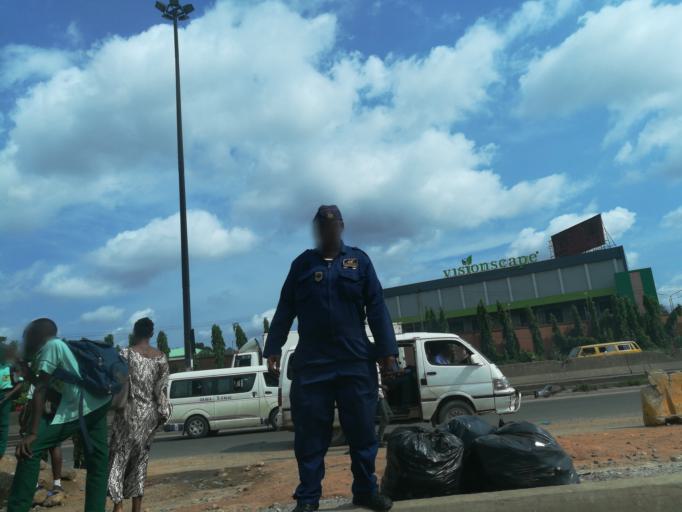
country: NG
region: Lagos
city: Oshodi
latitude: 6.5511
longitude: 3.3404
